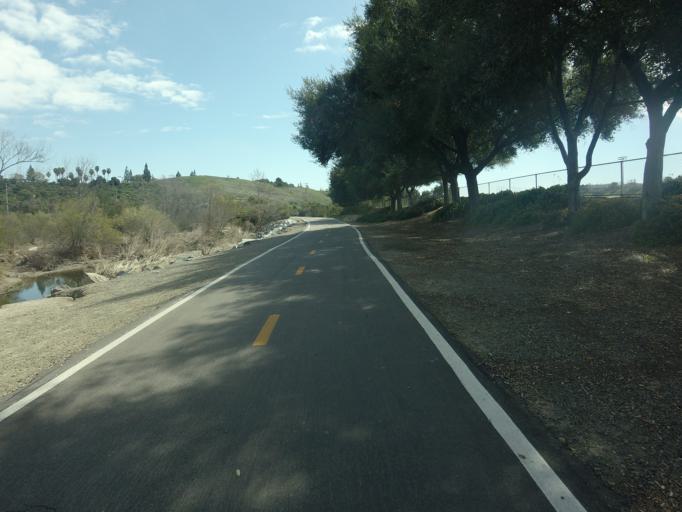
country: US
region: California
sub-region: Orange County
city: Aliso Viejo
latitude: 33.5685
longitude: -117.7180
